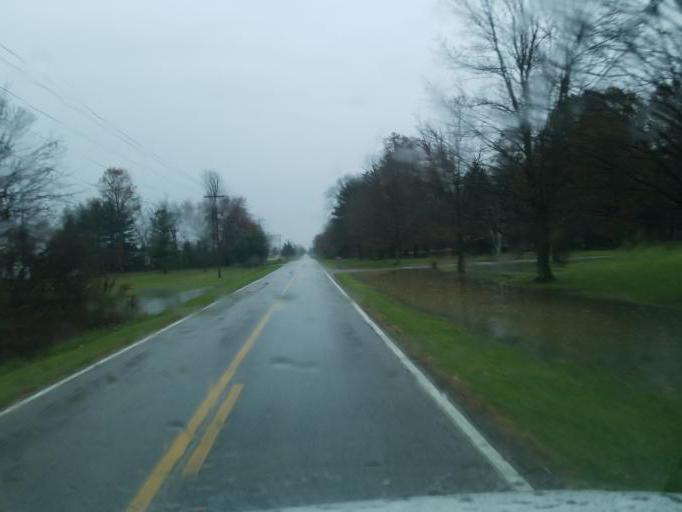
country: US
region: Ohio
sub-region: Delaware County
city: Sunbury
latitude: 40.3190
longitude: -82.8807
